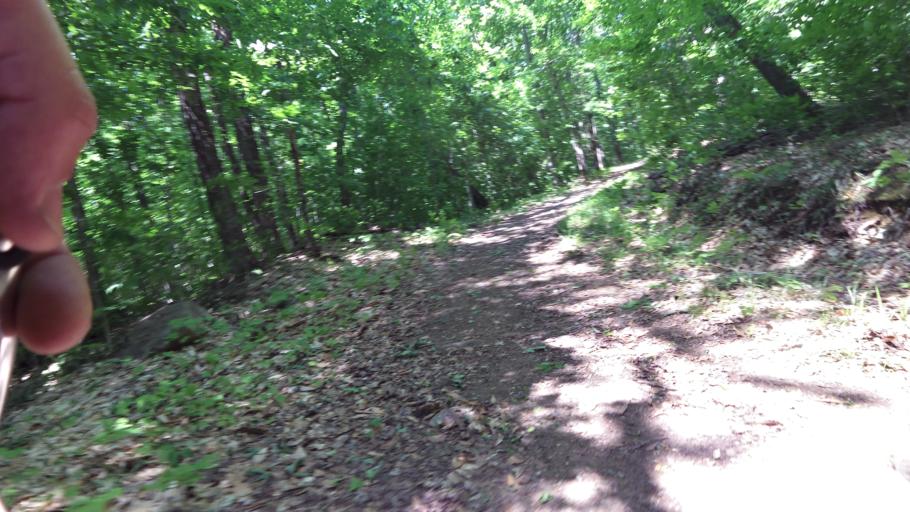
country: CA
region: Quebec
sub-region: Outaouais
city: Wakefield
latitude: 45.5878
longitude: -75.9667
